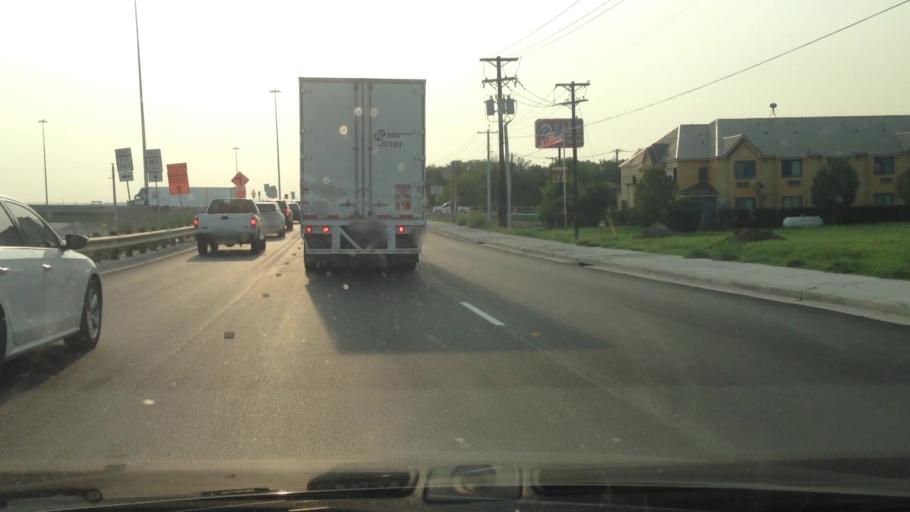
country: US
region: Texas
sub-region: Dallas County
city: Irving
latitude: 32.8364
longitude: -96.9090
